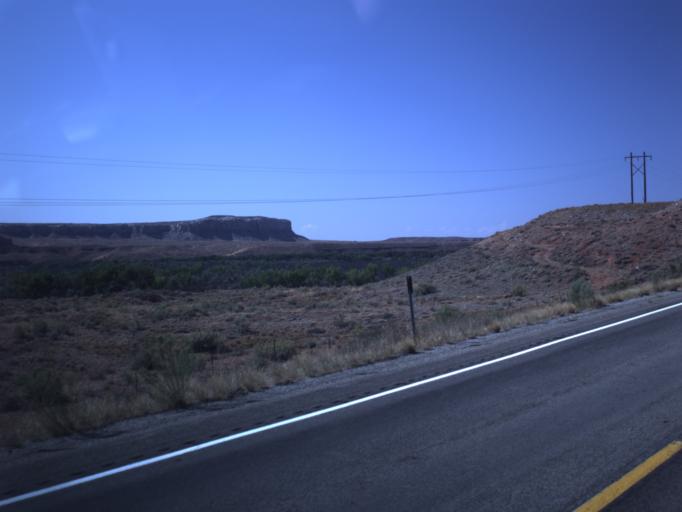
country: US
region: Utah
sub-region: San Juan County
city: Blanding
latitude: 37.2754
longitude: -109.5878
